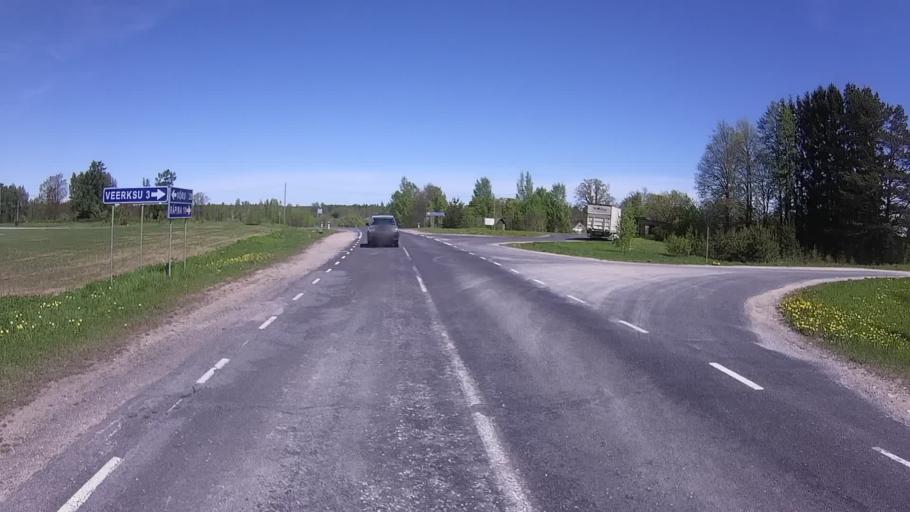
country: EE
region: Polvamaa
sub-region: Raepina vald
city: Rapina
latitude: 58.0361
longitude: 27.3927
